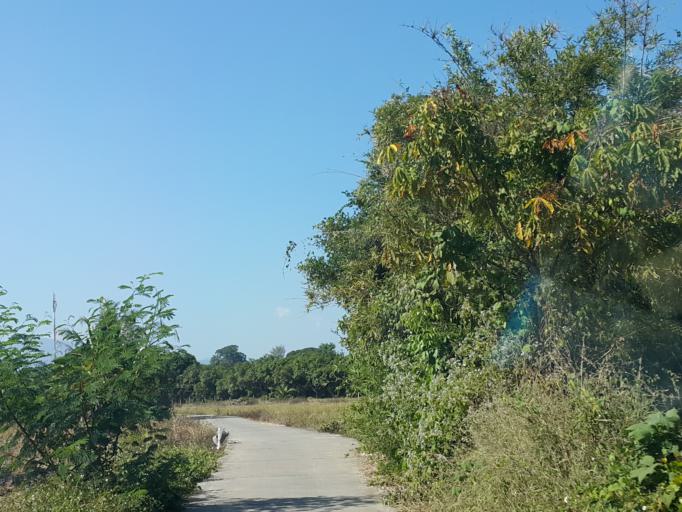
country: TH
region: Chiang Mai
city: San Sai
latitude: 18.8600
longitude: 98.9893
